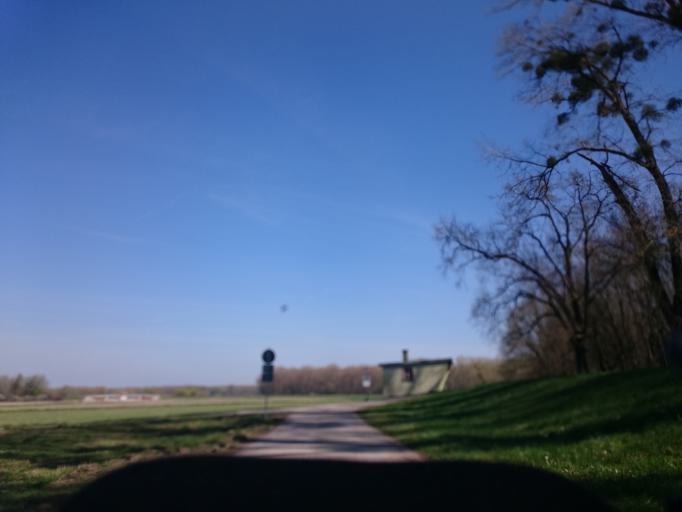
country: DE
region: Rheinland-Pfalz
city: Neupotz
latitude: 49.0826
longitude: 8.3303
